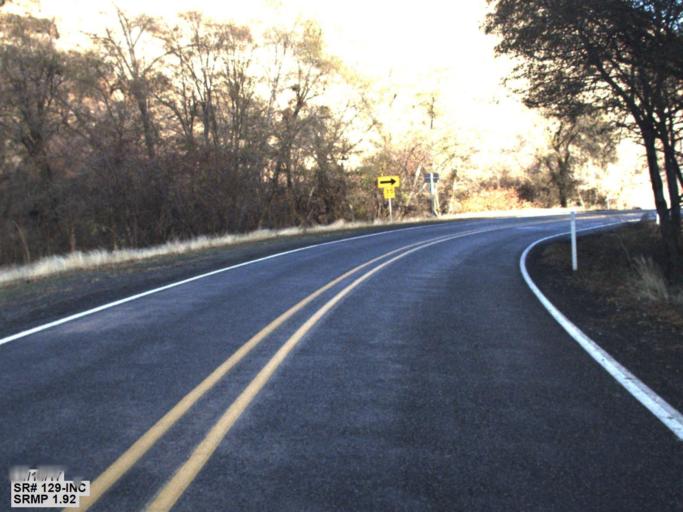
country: US
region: Washington
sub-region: Asotin County
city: Asotin
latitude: 46.0112
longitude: -117.2734
